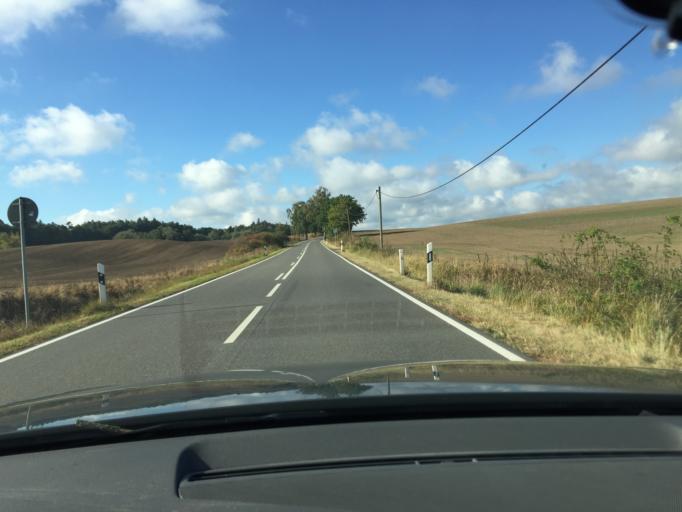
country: DE
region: Mecklenburg-Vorpommern
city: Krakow am See
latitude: 53.6846
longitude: 12.3150
